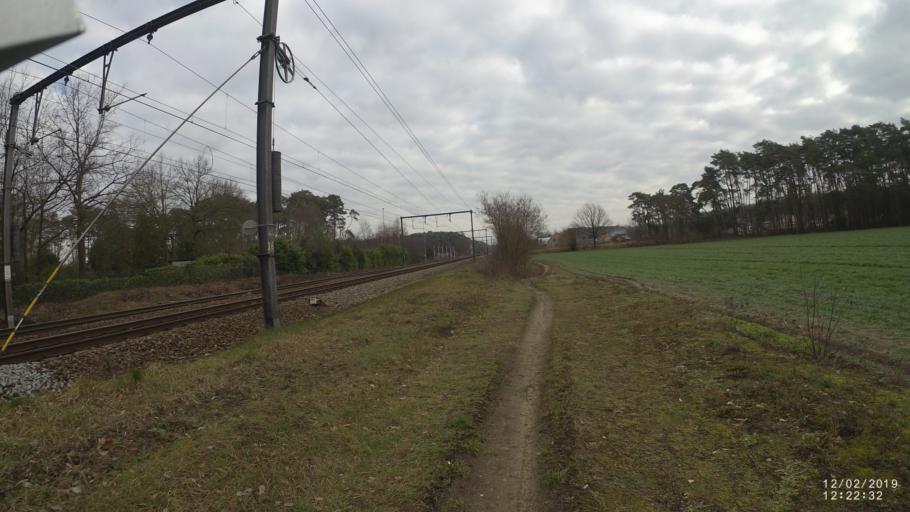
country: BE
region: Flanders
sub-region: Provincie Antwerpen
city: Herselt
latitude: 51.0070
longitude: 4.8945
